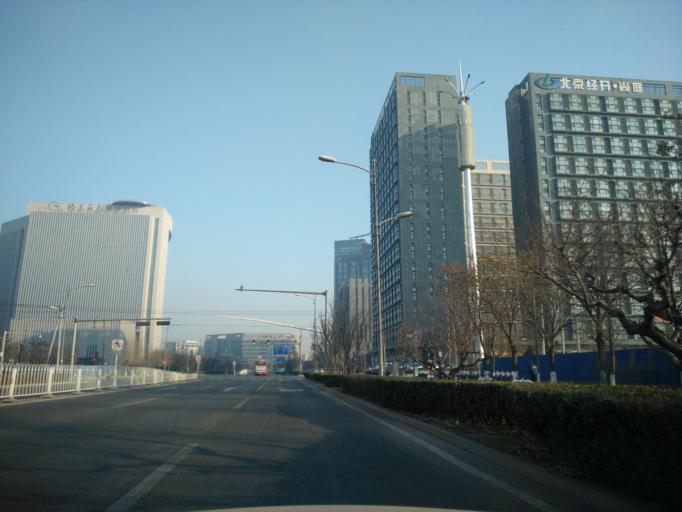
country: CN
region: Beijing
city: Jiugong
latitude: 39.7755
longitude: 116.5123
